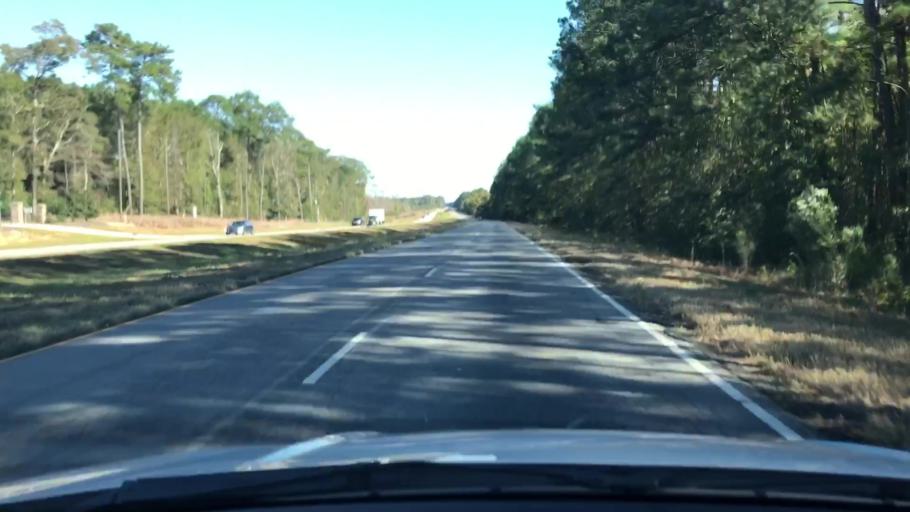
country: US
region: South Carolina
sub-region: Charleston County
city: Ravenel
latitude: 32.7575
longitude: -80.3778
